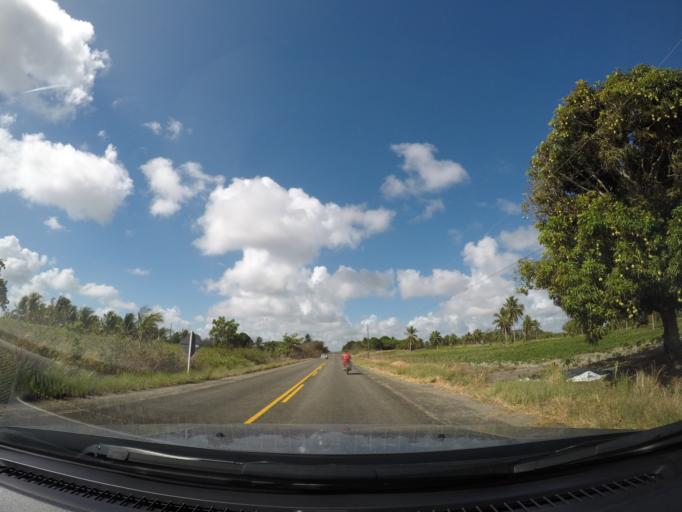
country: BR
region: Paraiba
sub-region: Pitimbu
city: Pitimbu
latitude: -7.4086
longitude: -34.8196
